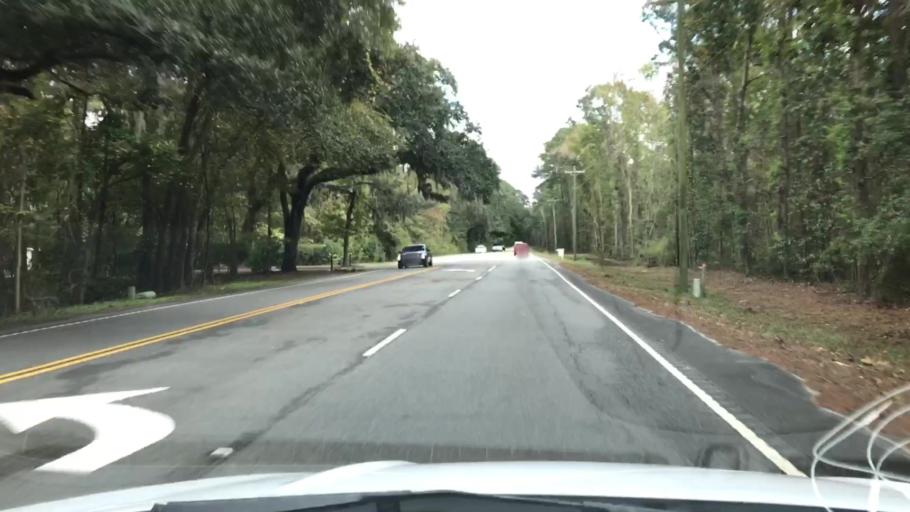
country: US
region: South Carolina
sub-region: Beaufort County
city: Bluffton
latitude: 32.2310
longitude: -80.9209
